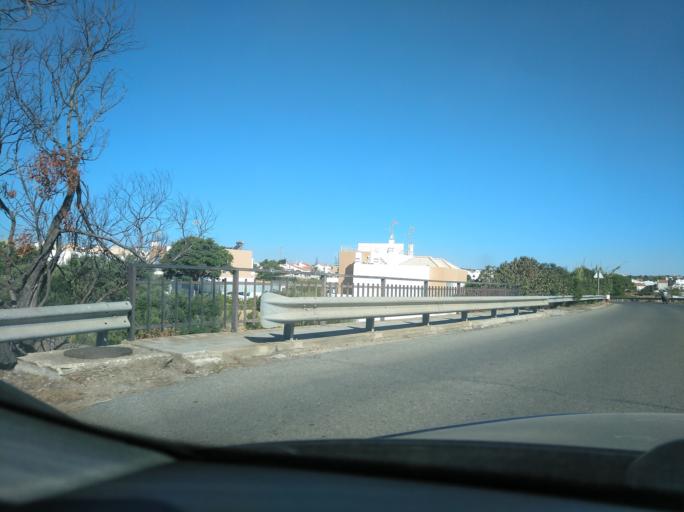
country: PT
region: Faro
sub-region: Vila Real de Santo Antonio
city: Monte Gordo
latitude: 37.1773
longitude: -7.5348
